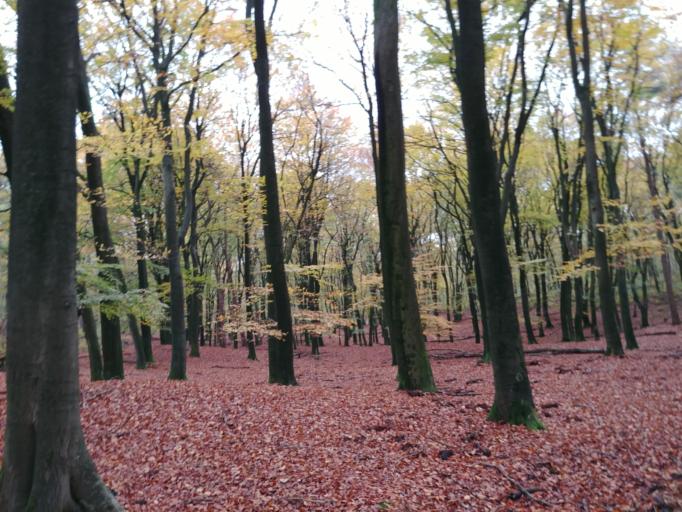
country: NL
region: Gelderland
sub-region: Gemeente Rheden
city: De Steeg
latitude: 52.0499
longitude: 6.0321
